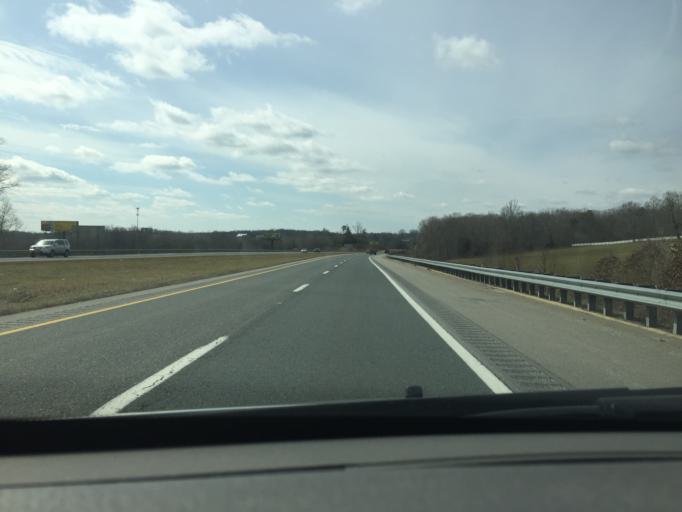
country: US
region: Virginia
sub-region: Campbell County
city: Timberlake
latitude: 37.3226
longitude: -79.2172
